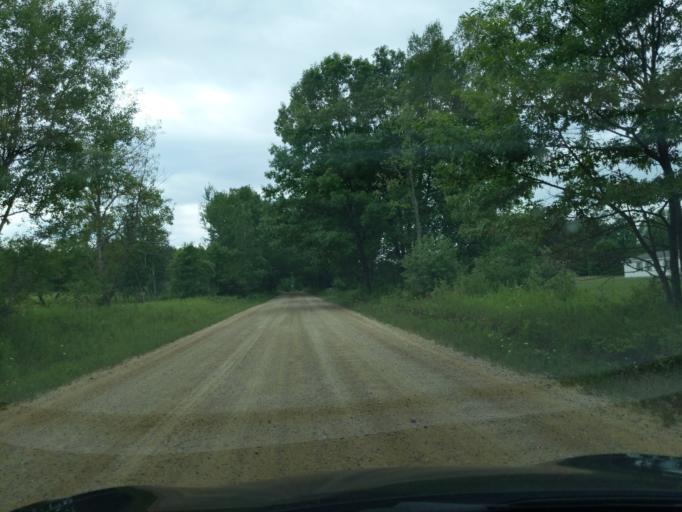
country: US
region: Michigan
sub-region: Clare County
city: Harrison
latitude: 44.0025
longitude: -84.9564
